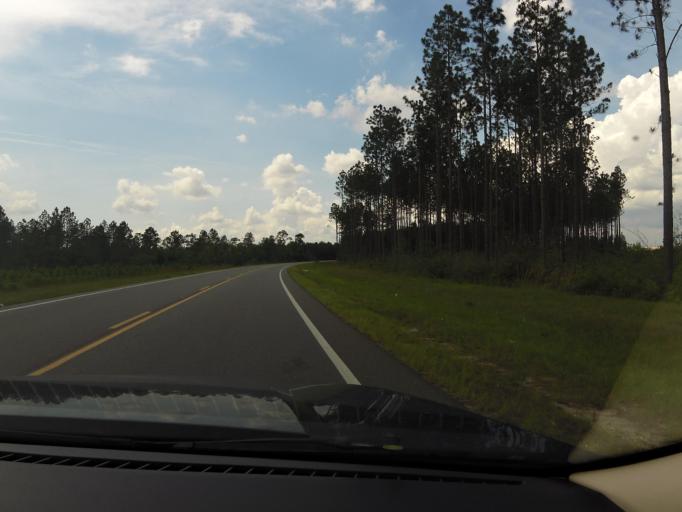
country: US
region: Florida
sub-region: Baker County
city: Macclenny
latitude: 30.2183
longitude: -82.0731
